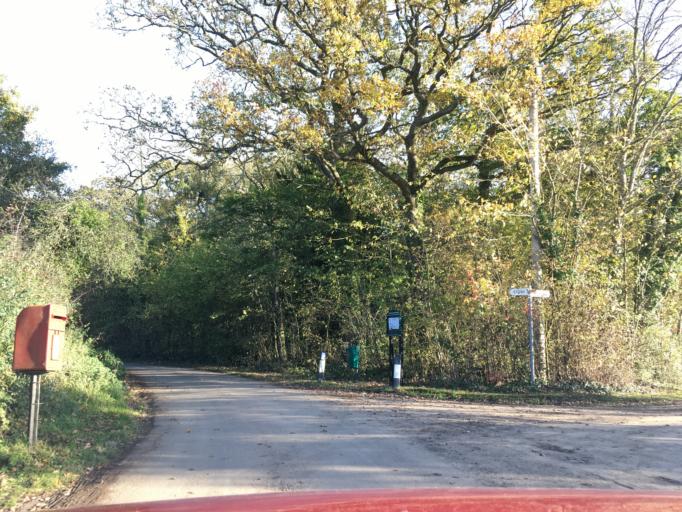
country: GB
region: England
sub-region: South Gloucestershire
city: Falfield
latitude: 51.6494
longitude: -2.4761
